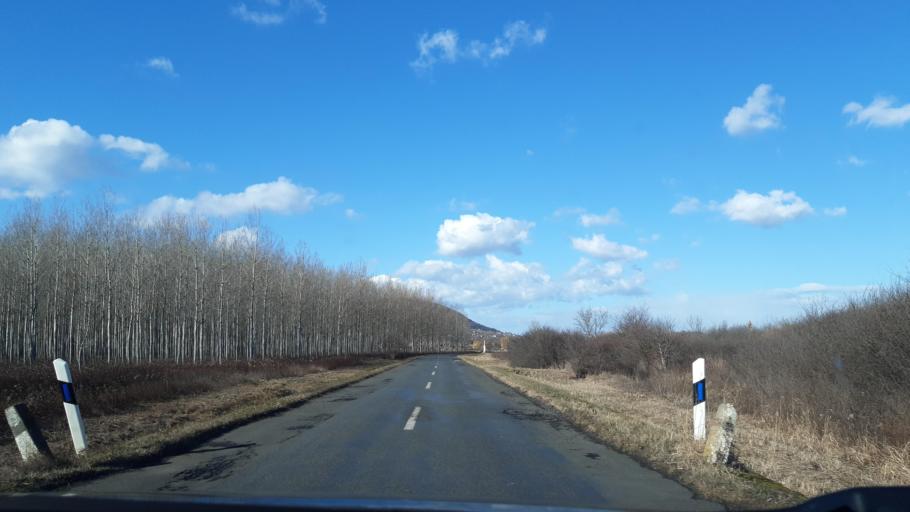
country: HU
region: Veszprem
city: Devecser
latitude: 47.1240
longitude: 17.4090
